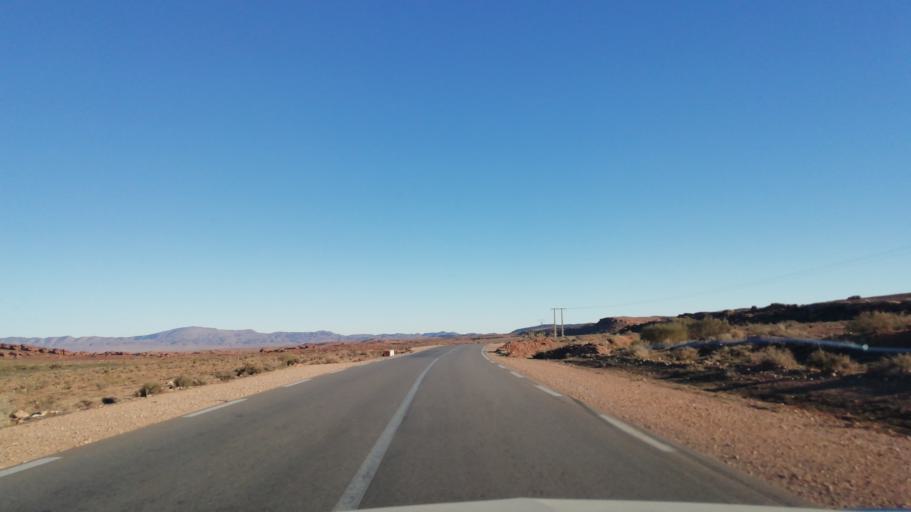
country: DZ
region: El Bayadh
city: El Abiodh Sidi Cheikh
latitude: 33.1730
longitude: 0.4547
